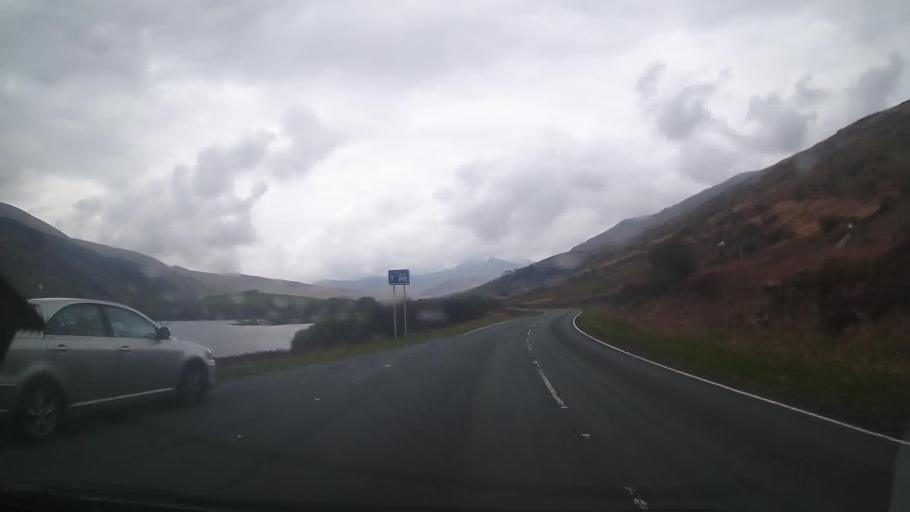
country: GB
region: Wales
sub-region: Gwynedd
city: Blaenau-Ffestiniog
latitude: 53.0993
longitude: -3.9331
